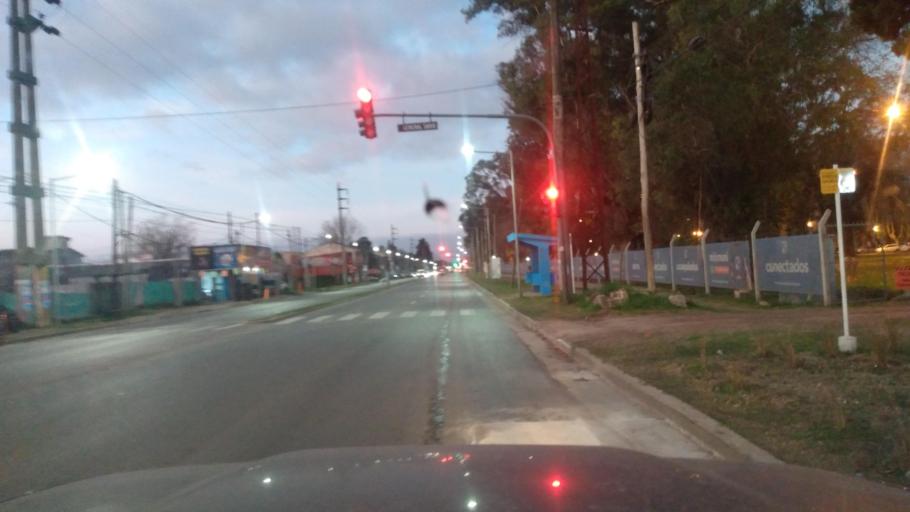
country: AR
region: Buenos Aires
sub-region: Partido de Pilar
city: Pilar
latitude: -34.4386
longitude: -58.8945
